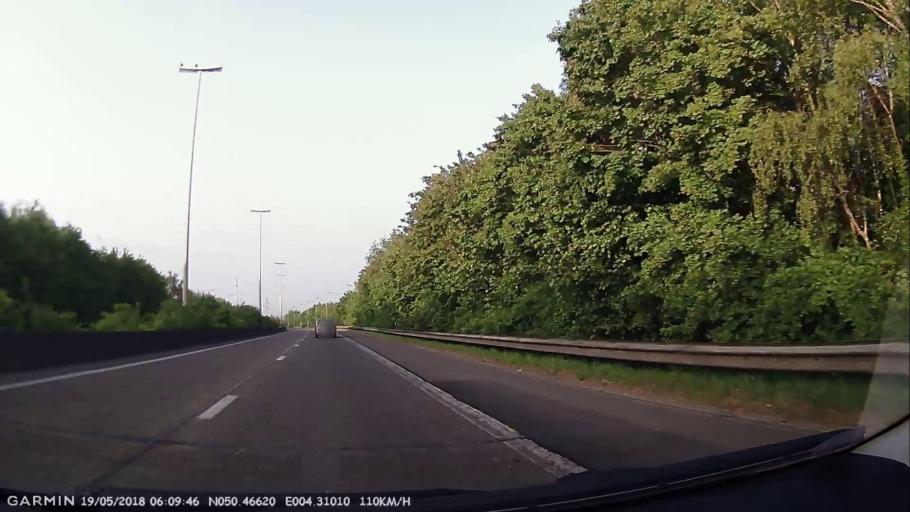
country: BE
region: Wallonia
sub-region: Province du Hainaut
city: Chapelle-lez-Herlaimont
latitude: 50.4661
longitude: 4.3099
